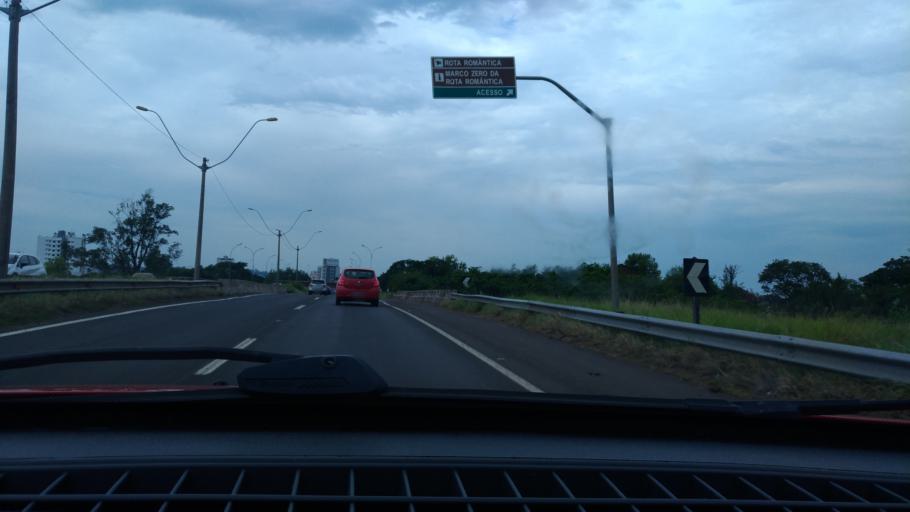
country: BR
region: Rio Grande do Sul
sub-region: Sao Leopoldo
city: Sao Leopoldo
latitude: -29.7572
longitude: -51.1519
